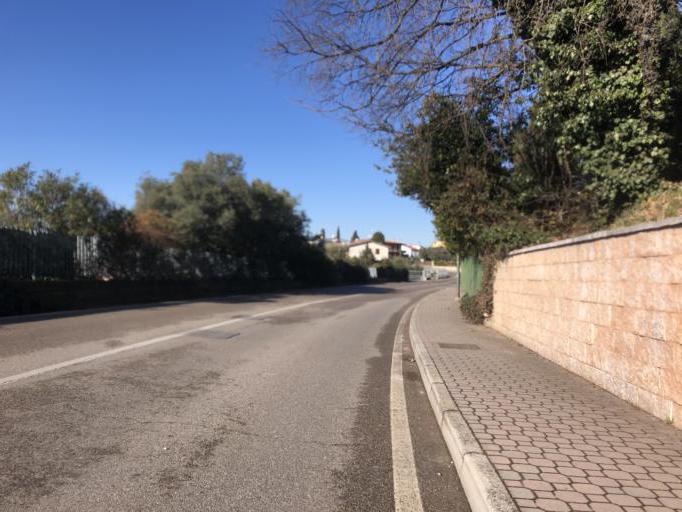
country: IT
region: Veneto
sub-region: Provincia di Verona
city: Sona
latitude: 45.4355
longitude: 10.8291
